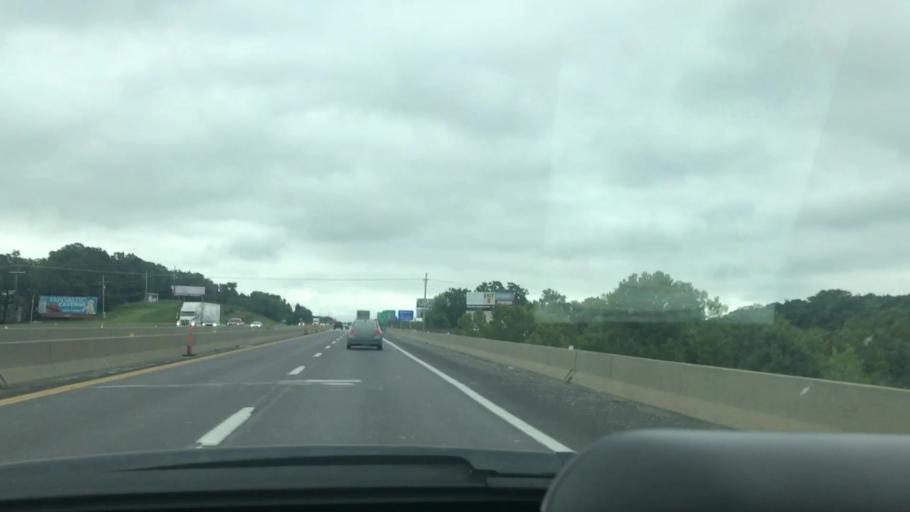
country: US
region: Missouri
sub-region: Jasper County
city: Joplin
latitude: 37.0306
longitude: -94.5237
